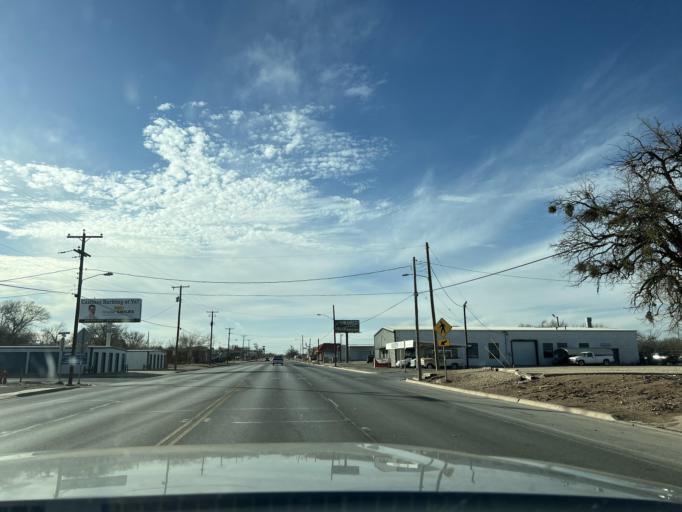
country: US
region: Texas
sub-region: Scurry County
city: Snyder
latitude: 32.7172
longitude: -100.9231
